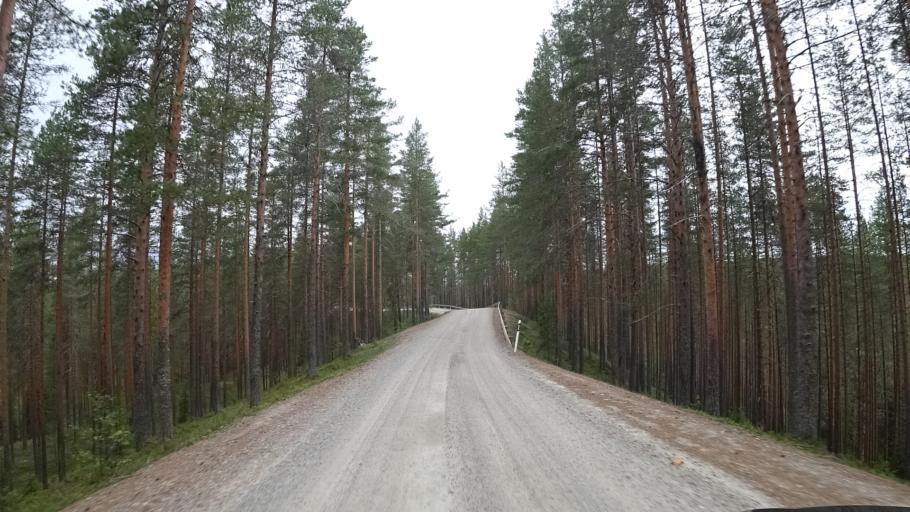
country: FI
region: North Karelia
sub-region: Pielisen Karjala
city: Lieksa
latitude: 63.2109
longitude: 30.4170
